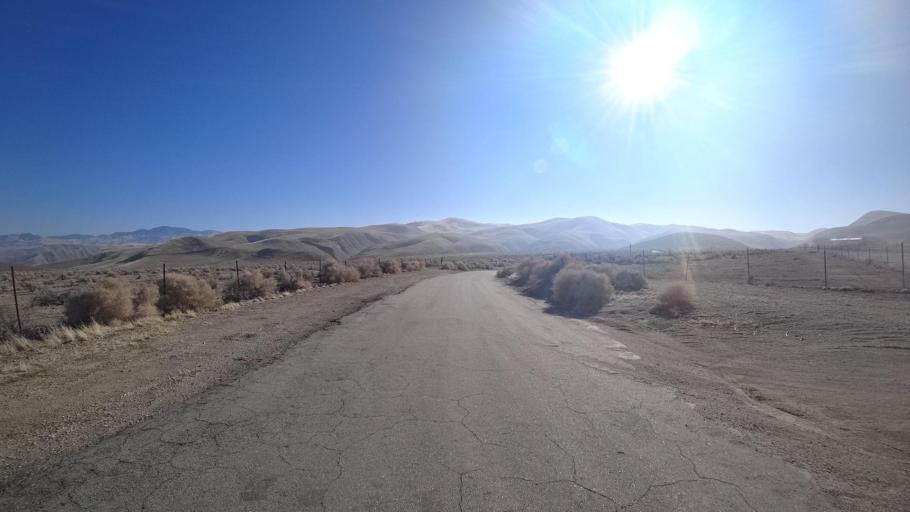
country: US
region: California
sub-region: Kern County
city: Maricopa
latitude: 34.9916
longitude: -119.3914
